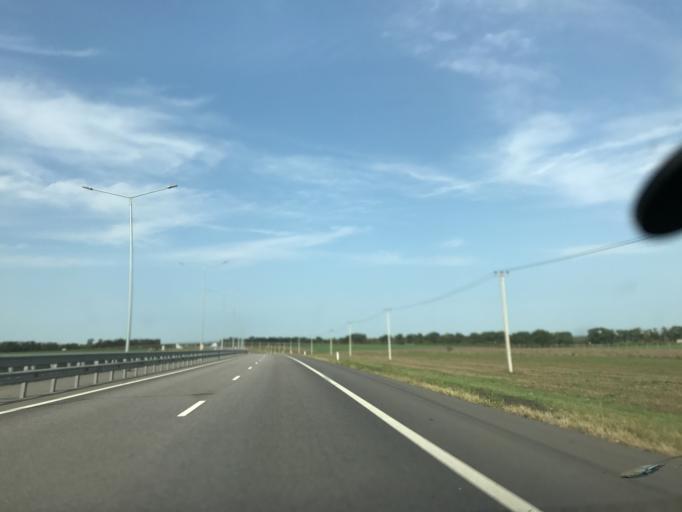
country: RU
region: Voronezj
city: Podkletnoye
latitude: 51.5244
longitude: 39.5108
